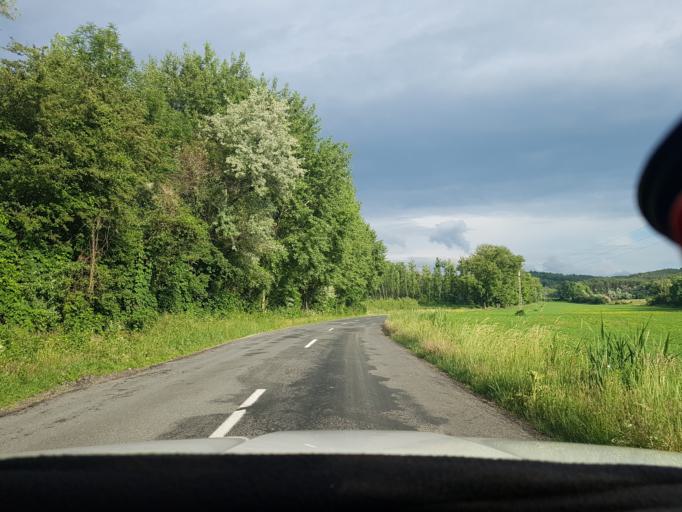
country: HU
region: Komarom-Esztergom
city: Labatlan
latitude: 47.7344
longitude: 18.5262
